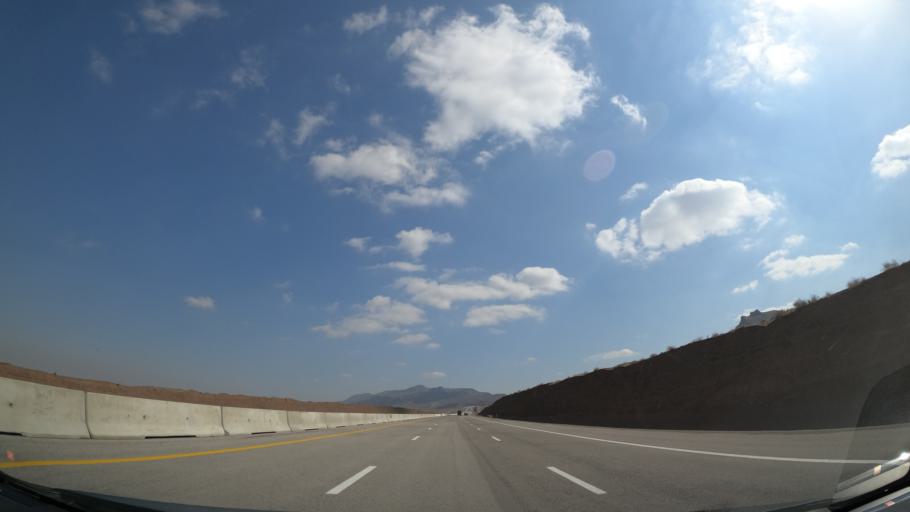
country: IR
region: Alborz
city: Eshtehard
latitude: 35.7050
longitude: 50.6123
